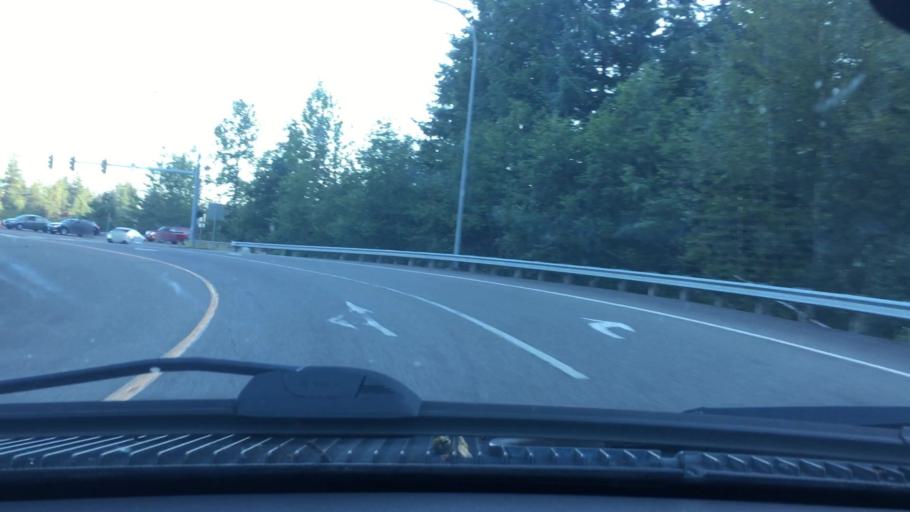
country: US
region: Washington
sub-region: King County
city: Maple Valley
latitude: 47.3946
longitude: -122.0493
